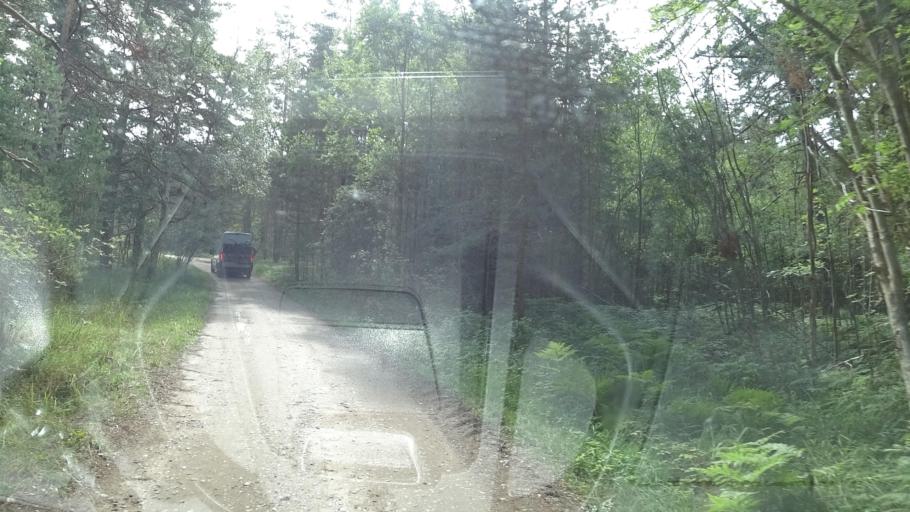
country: LV
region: Ventspils
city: Ventspils
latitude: 57.4876
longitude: 21.6478
